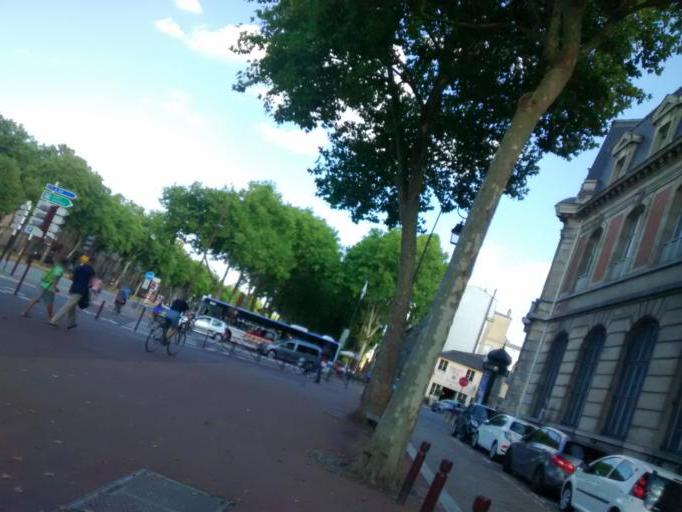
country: FR
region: Ile-de-France
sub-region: Departement des Yvelines
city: Versailles
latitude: 48.8016
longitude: 2.1310
